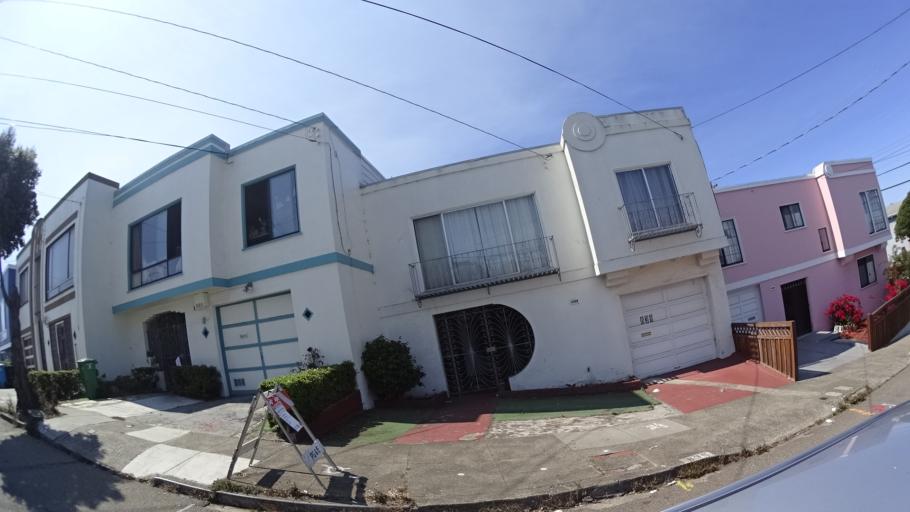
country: US
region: California
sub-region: San Mateo County
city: Daly City
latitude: 37.7180
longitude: -122.4591
